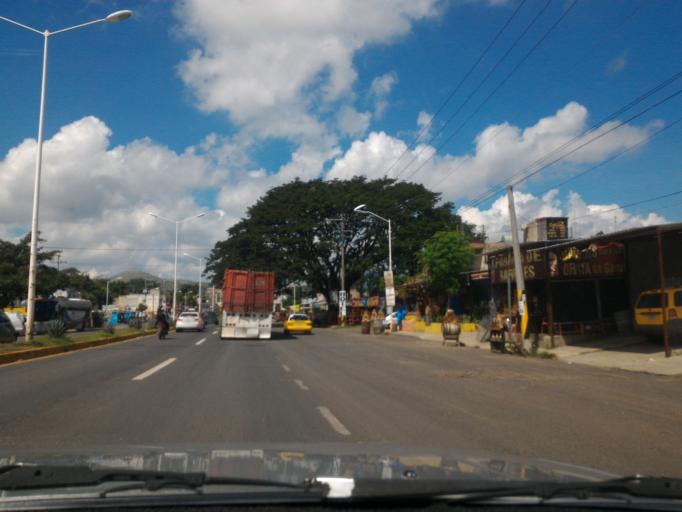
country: MX
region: Jalisco
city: Tequila
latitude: 20.8799
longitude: -103.8264
